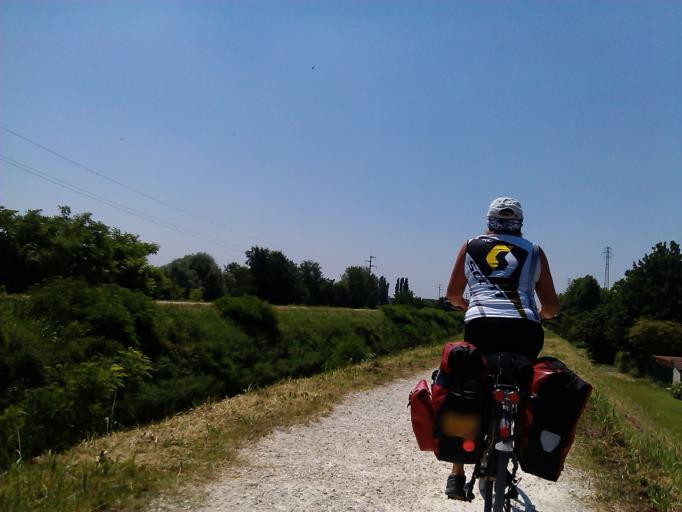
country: IT
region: Veneto
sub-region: Provincia di Padova
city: Camposampiero
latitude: 45.5689
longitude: 11.9395
